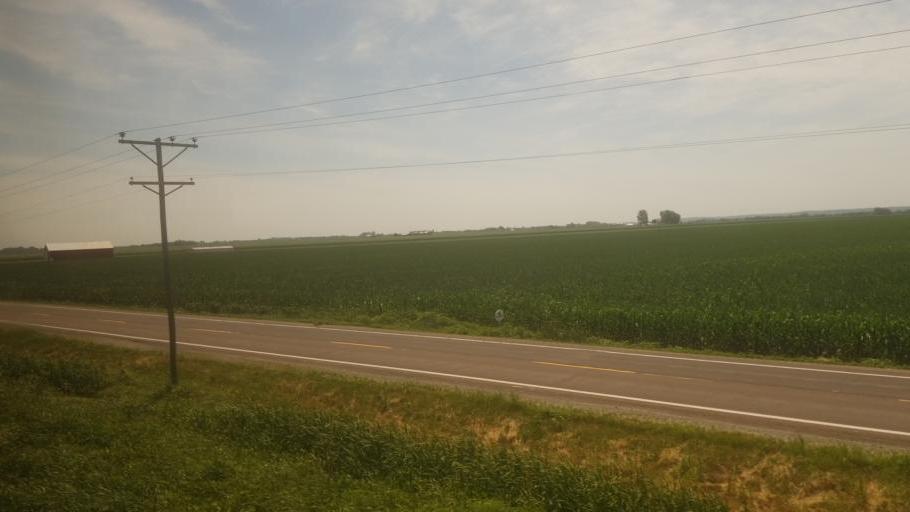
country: US
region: Missouri
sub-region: Carroll County
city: Carrollton
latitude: 39.3072
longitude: -93.6598
